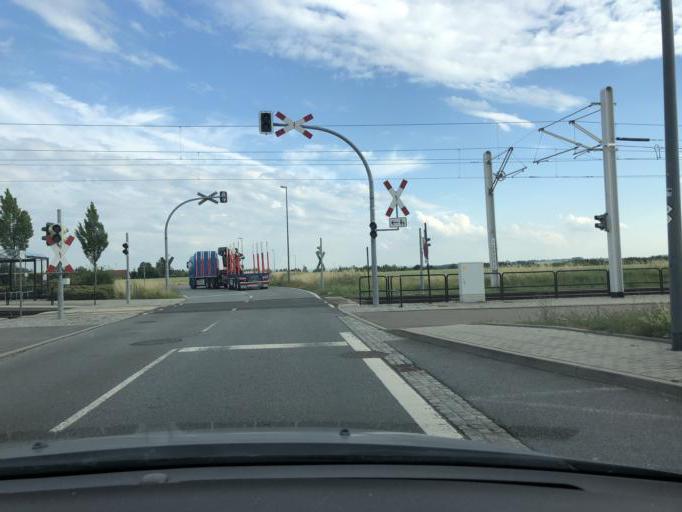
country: DE
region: Saxony
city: Freital
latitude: 51.0409
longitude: 13.6254
